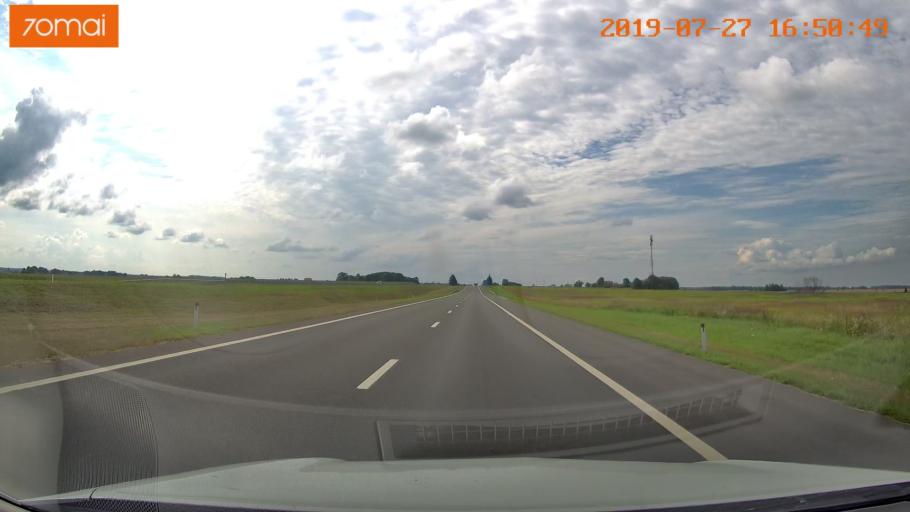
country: RU
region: Kaliningrad
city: Gvardeysk
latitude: 54.6795
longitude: 20.9036
